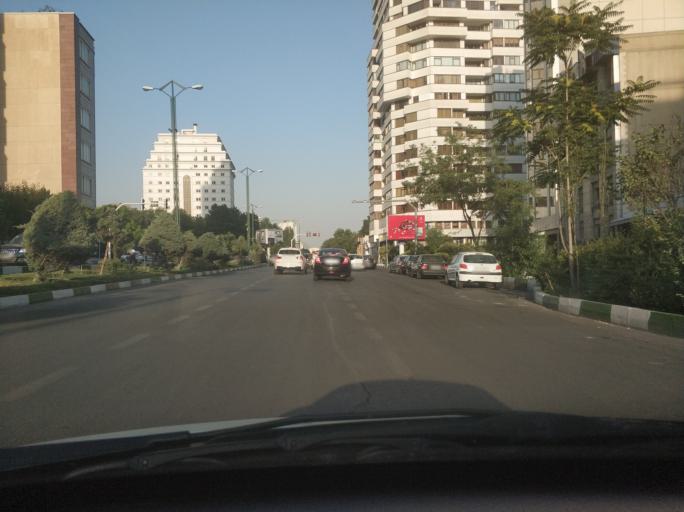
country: IR
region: Tehran
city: Tajrish
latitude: 35.8015
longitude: 51.4604
